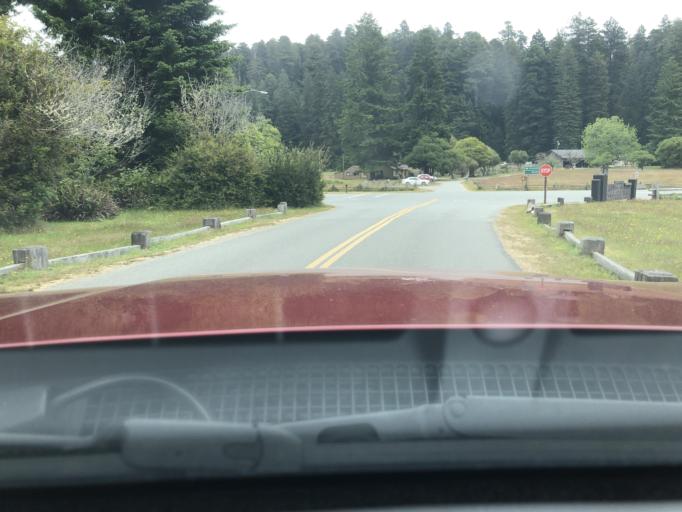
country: US
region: California
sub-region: Humboldt County
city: Westhaven-Moonstone
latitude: 41.3640
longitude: -124.0216
